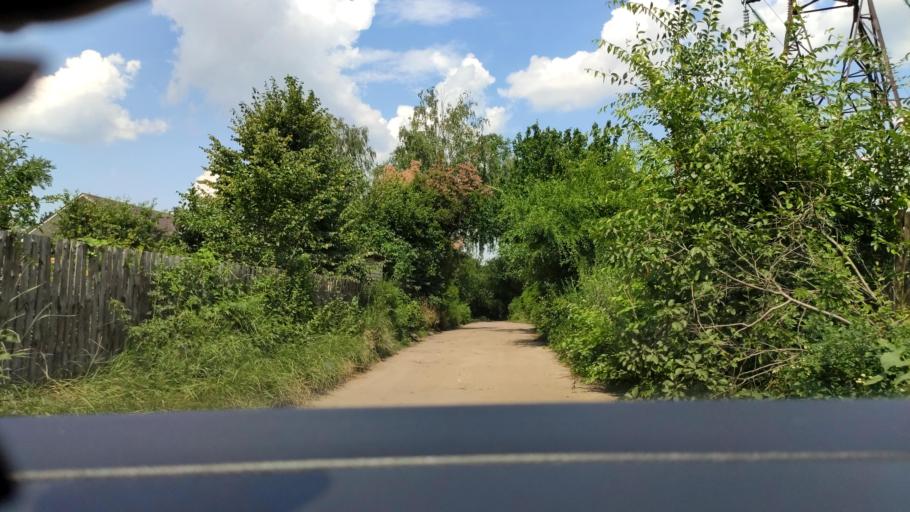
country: RU
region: Voronezj
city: Maslovka
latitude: 51.6059
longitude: 39.2862
